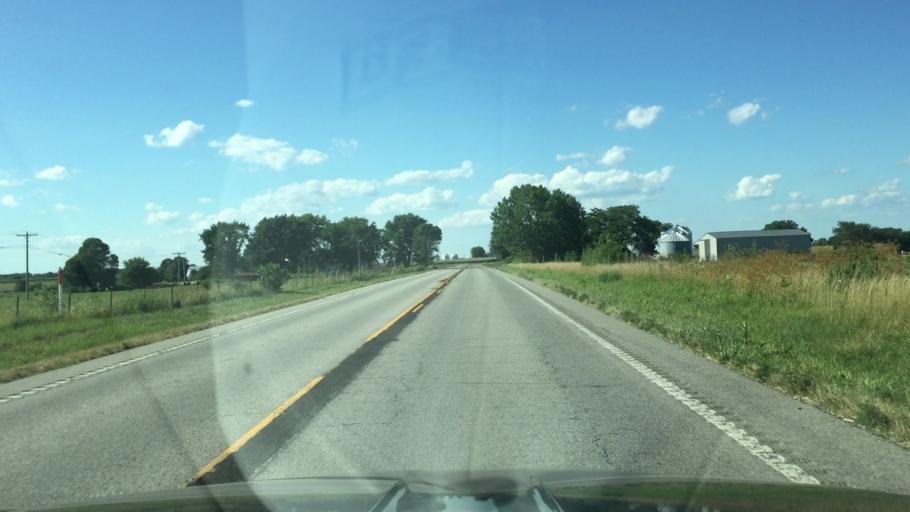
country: US
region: Missouri
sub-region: Moniteau County
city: Tipton
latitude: 38.6042
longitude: -92.7897
